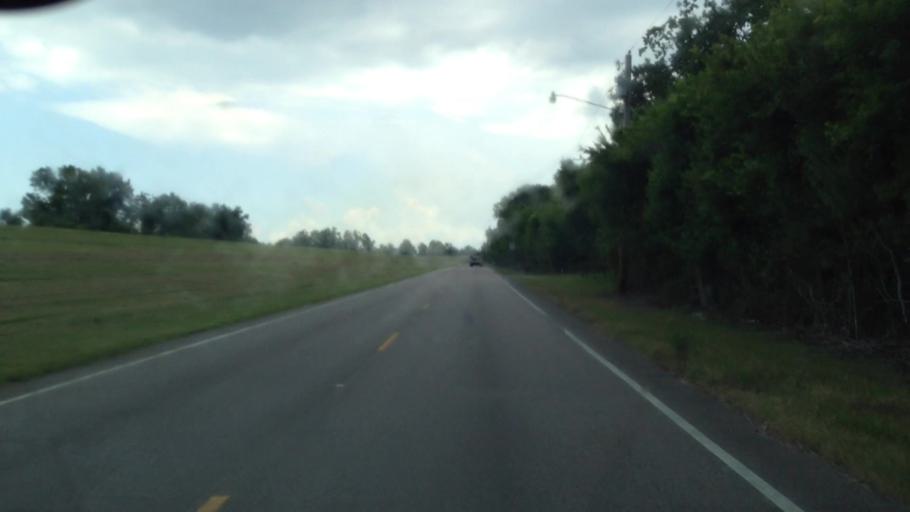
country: US
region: Louisiana
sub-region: Jefferson Parish
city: Bridge City
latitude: 29.9446
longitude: -90.1618
